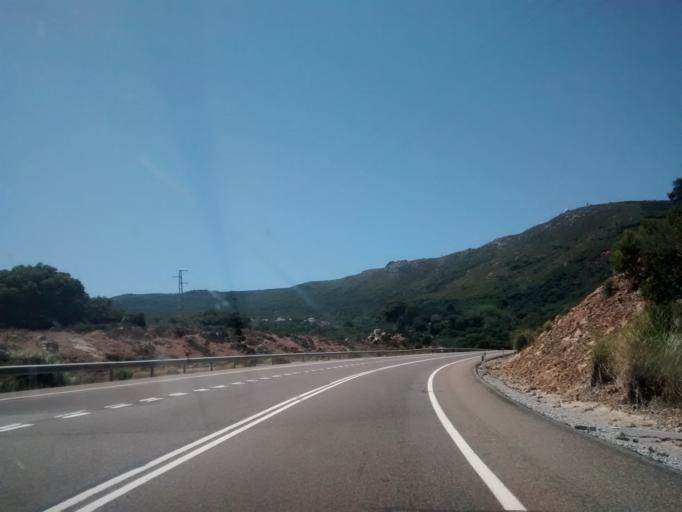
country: ES
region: Andalusia
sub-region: Provincia de Cadiz
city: Tarifa
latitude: 36.0689
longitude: -5.5266
